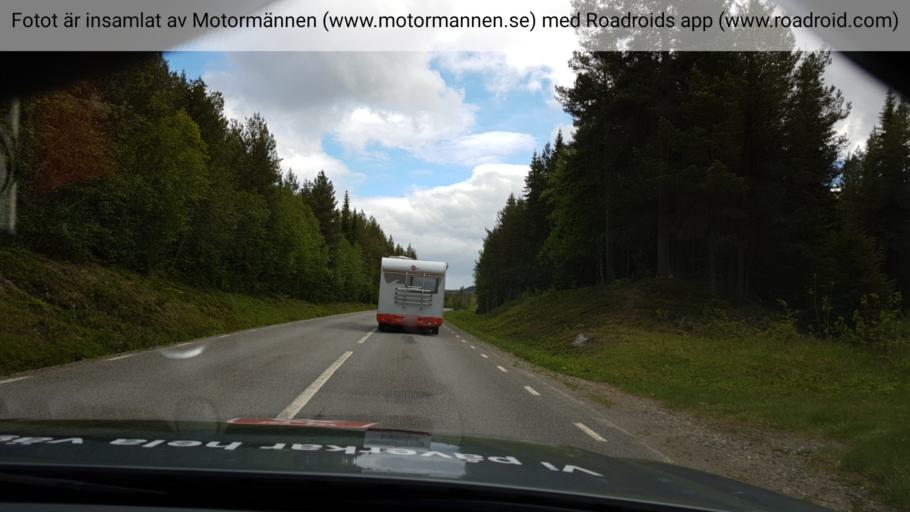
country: NO
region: Nord-Trondelag
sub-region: Lierne
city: Sandvika
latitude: 64.3955
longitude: 14.5117
